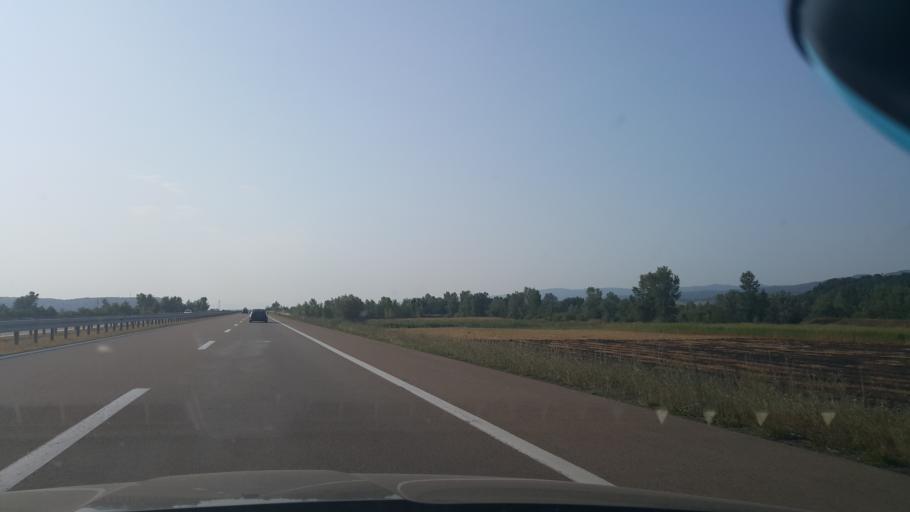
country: RS
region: Central Serbia
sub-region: Jablanicki Okrug
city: Leskovac
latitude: 43.0606
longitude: 21.9717
